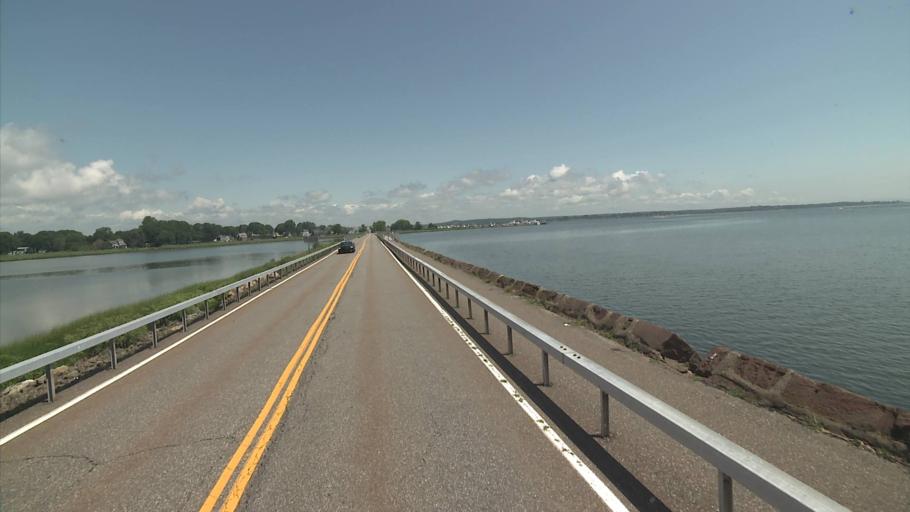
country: US
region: Connecticut
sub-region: Middlesex County
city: Old Saybrook Center
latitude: 41.2767
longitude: -72.3555
